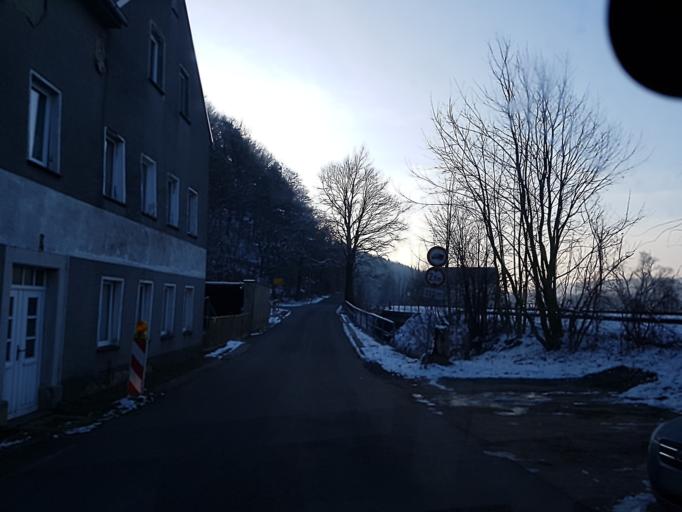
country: DE
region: Saxony
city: Grossweitzschen
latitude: 51.1558
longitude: 13.0092
